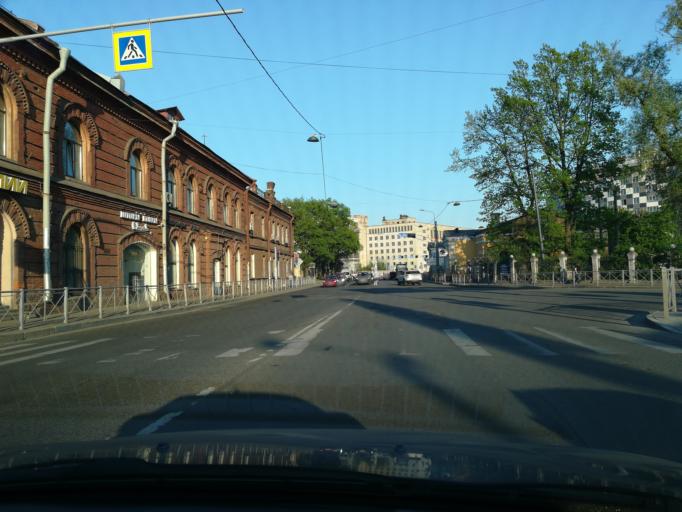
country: RU
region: St.-Petersburg
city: Vasyl'evsky Ostrov
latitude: 59.9530
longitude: 30.2622
